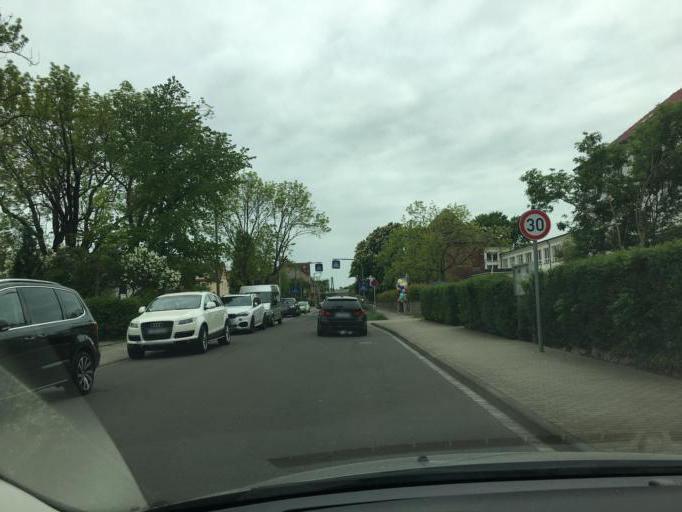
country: DE
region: Saxony
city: Rackwitz
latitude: 51.4035
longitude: 12.4128
